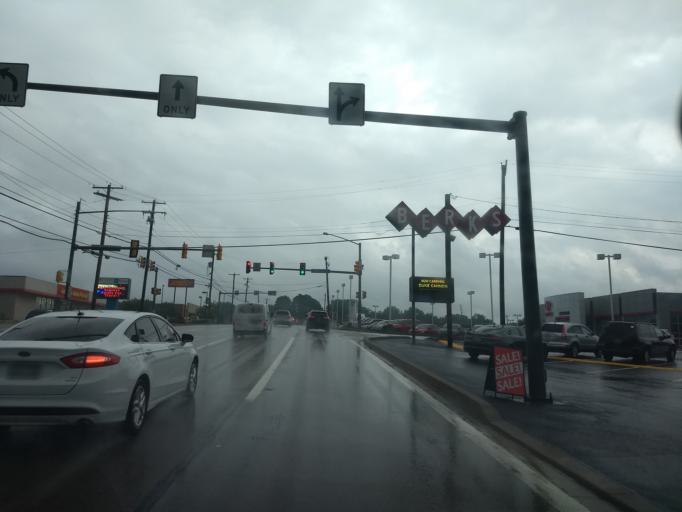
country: US
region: Pennsylvania
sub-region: Westmoreland County
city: Irwin
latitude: 40.3336
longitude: -79.7432
